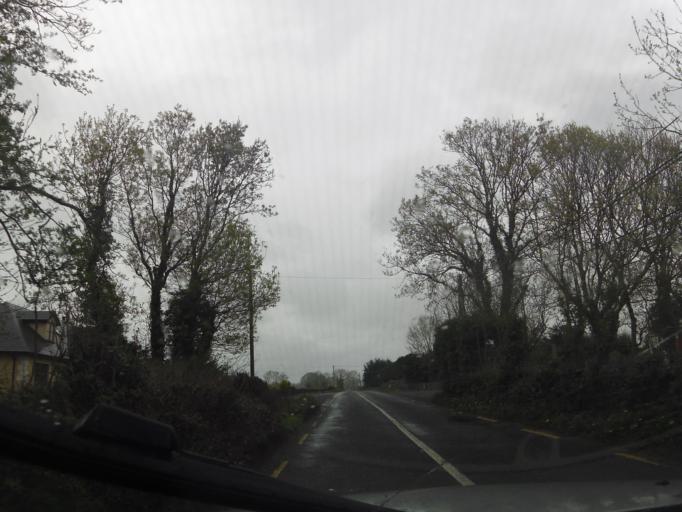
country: IE
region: Connaught
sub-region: Maigh Eo
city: Ballinrobe
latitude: 53.5650
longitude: -9.2379
